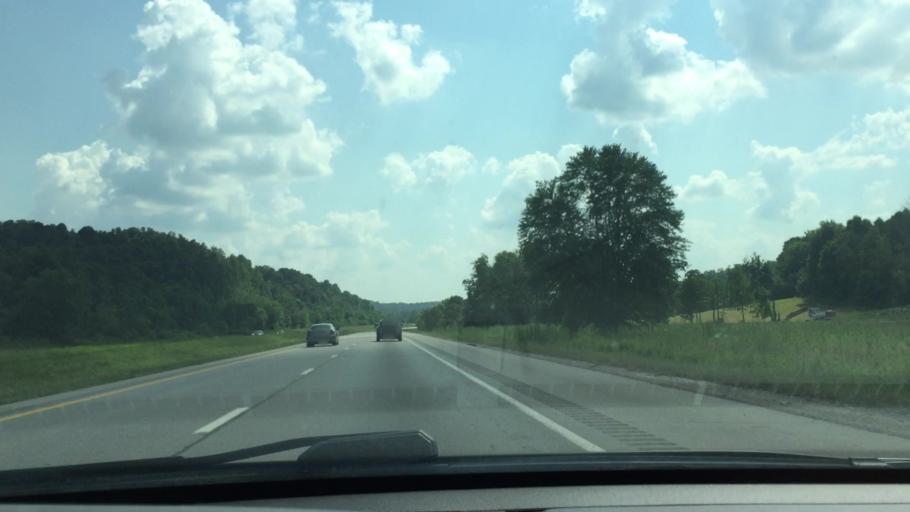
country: US
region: Ohio
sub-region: Guernsey County
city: Byesville
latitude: 40.0113
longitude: -81.4854
